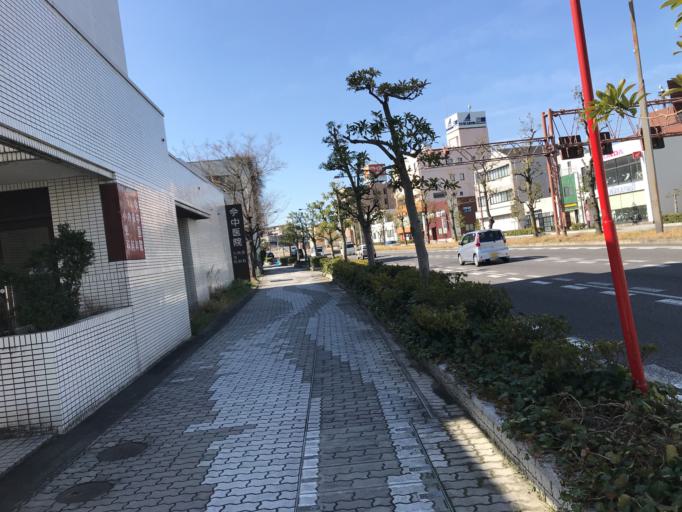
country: JP
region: Mie
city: Tsu-shi
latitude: 34.7282
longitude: 136.5117
